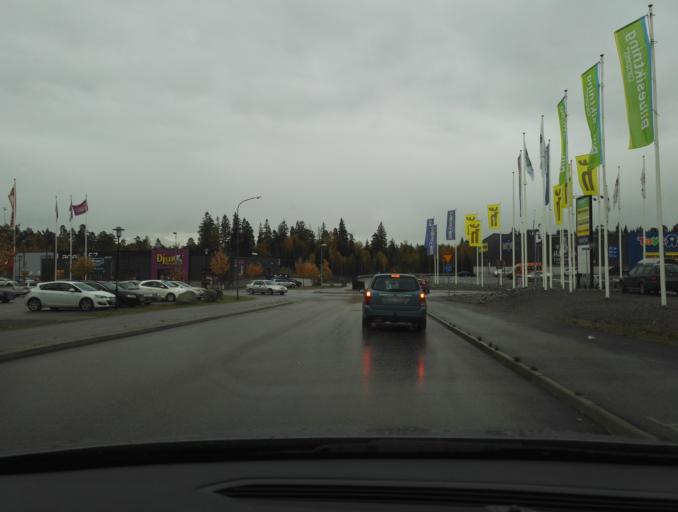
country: SE
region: Kronoberg
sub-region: Vaxjo Kommun
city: Vaexjoe
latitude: 56.8780
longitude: 14.7697
